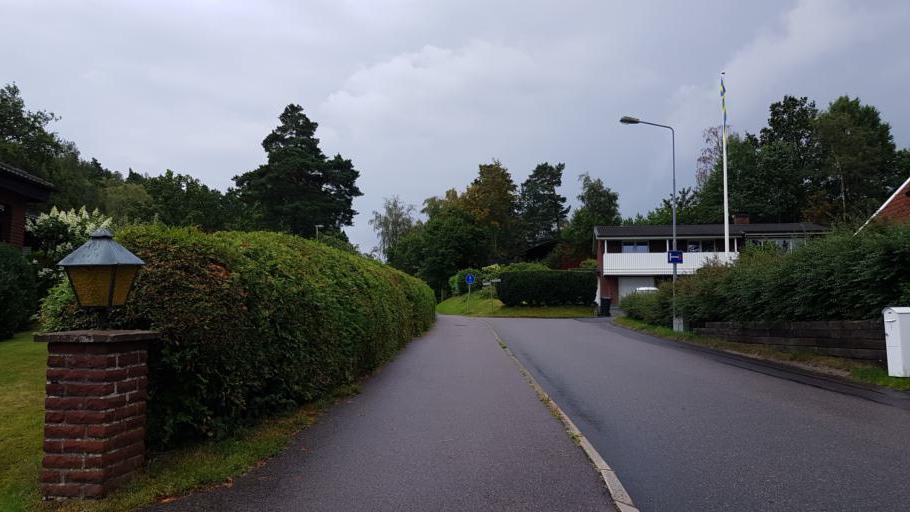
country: SE
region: Vaestra Goetaland
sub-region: Harryda Kommun
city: Molnlycke
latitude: 57.6532
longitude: 12.1107
